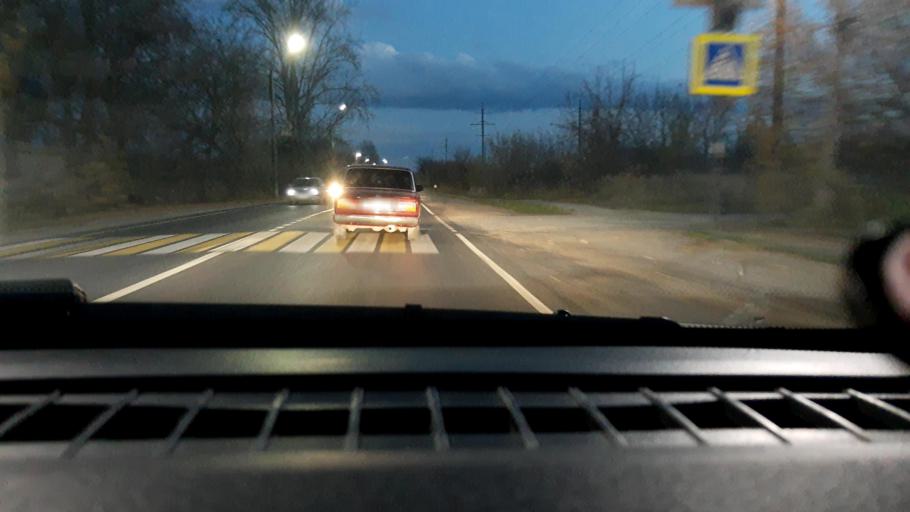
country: RU
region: Nizjnij Novgorod
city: Novaya Balakhna
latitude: 56.4843
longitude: 43.5996
